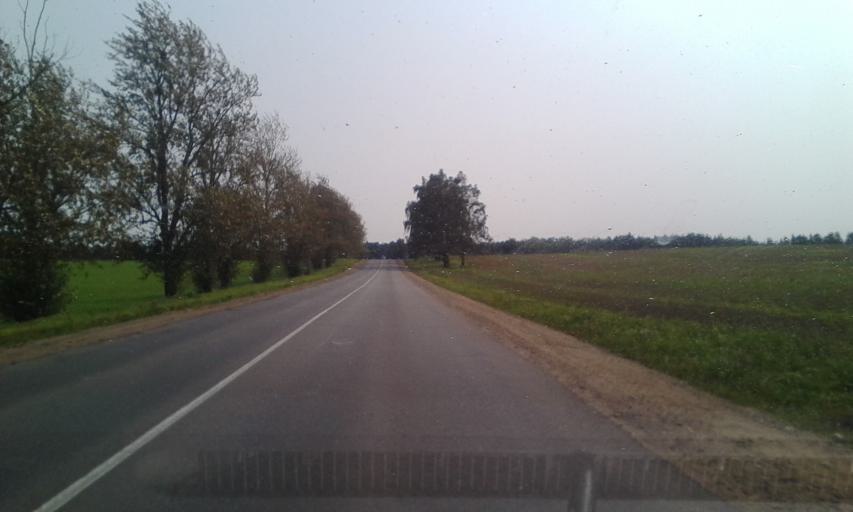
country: BY
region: Minsk
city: Hatava
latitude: 53.8193
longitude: 27.6397
